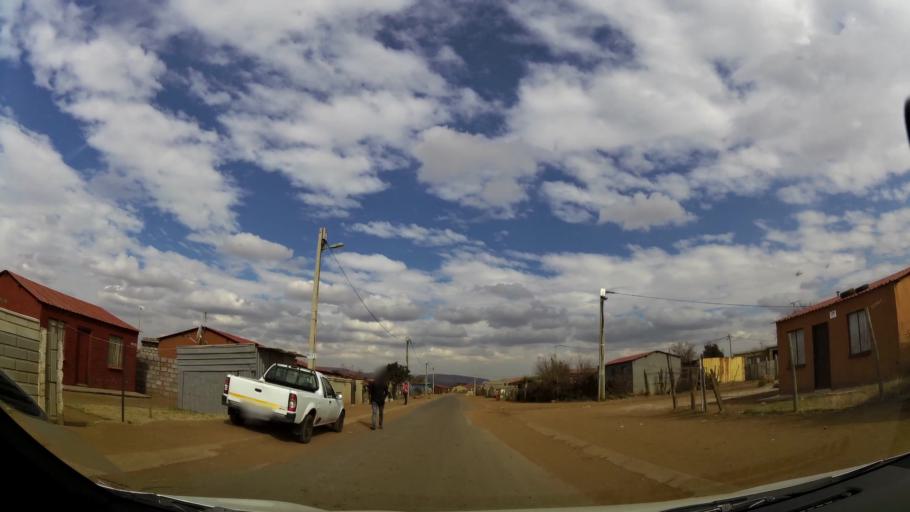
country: ZA
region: Gauteng
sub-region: Ekurhuleni Metropolitan Municipality
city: Germiston
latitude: -26.4098
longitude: 28.1611
